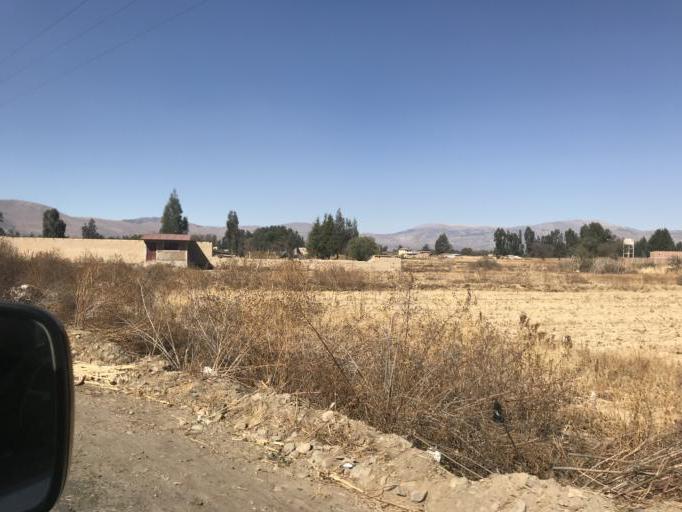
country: BO
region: Cochabamba
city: Punata
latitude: -17.5550
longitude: -65.8575
